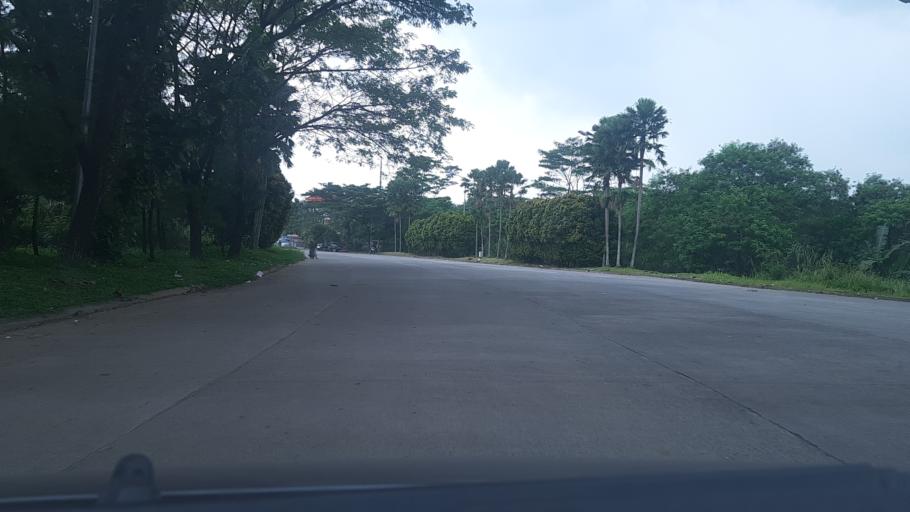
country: ID
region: West Java
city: Citeureup
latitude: -6.5750
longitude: 106.8905
